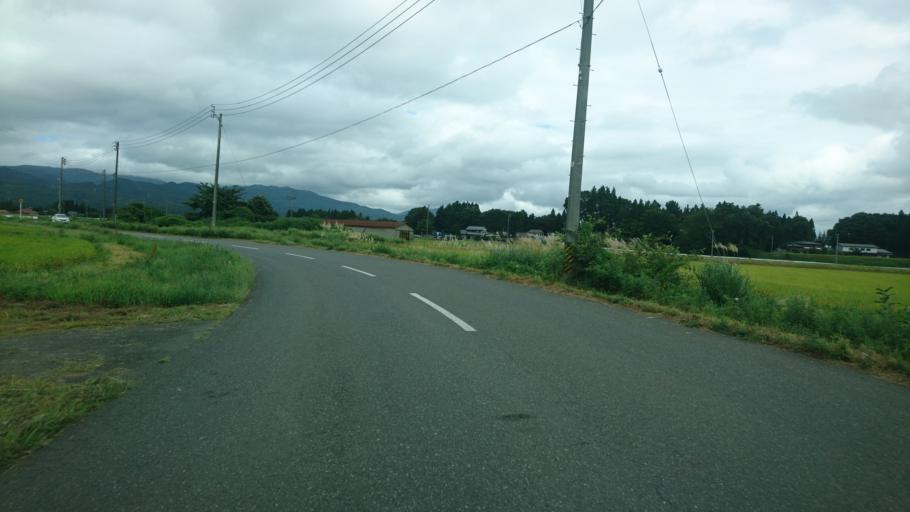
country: JP
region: Iwate
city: Kitakami
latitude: 39.3019
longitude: 140.9943
